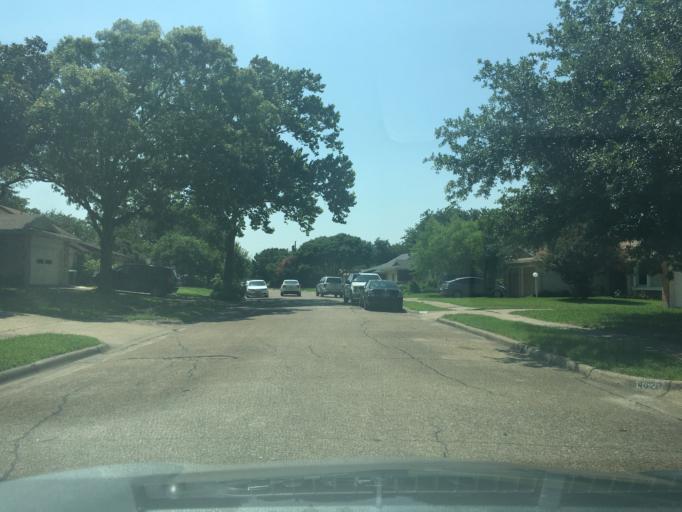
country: US
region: Texas
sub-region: Dallas County
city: Richardson
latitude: 32.9276
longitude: -96.7034
